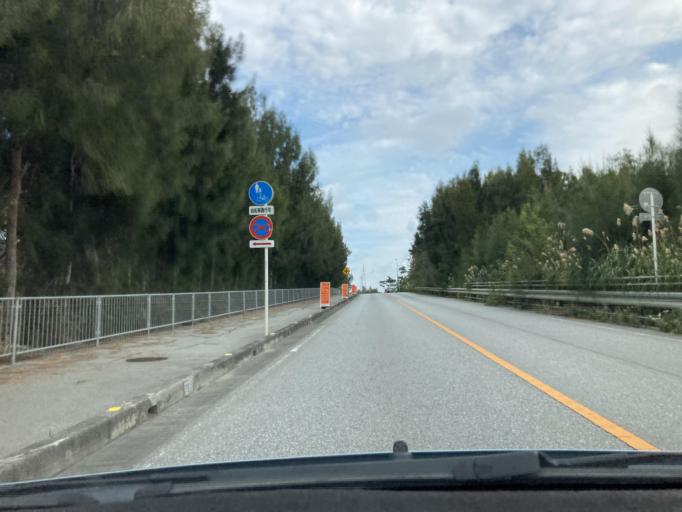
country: JP
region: Okinawa
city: Ishikawa
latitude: 26.4961
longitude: 127.8594
